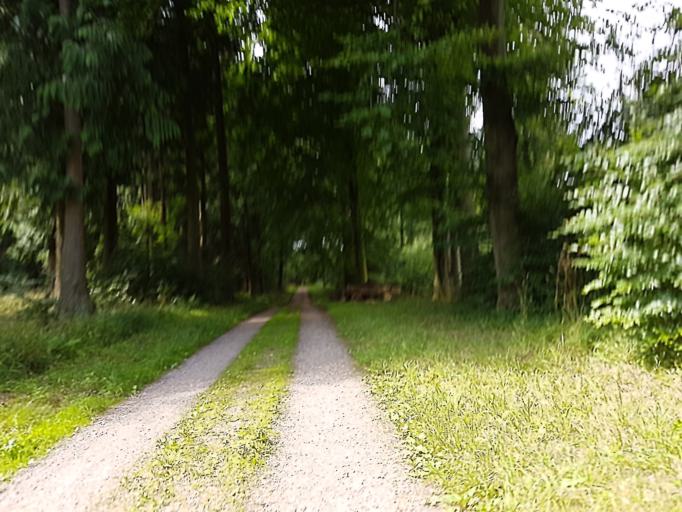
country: DK
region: Capital Region
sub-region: Fureso Kommune
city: Farum
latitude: 55.7971
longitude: 12.3500
